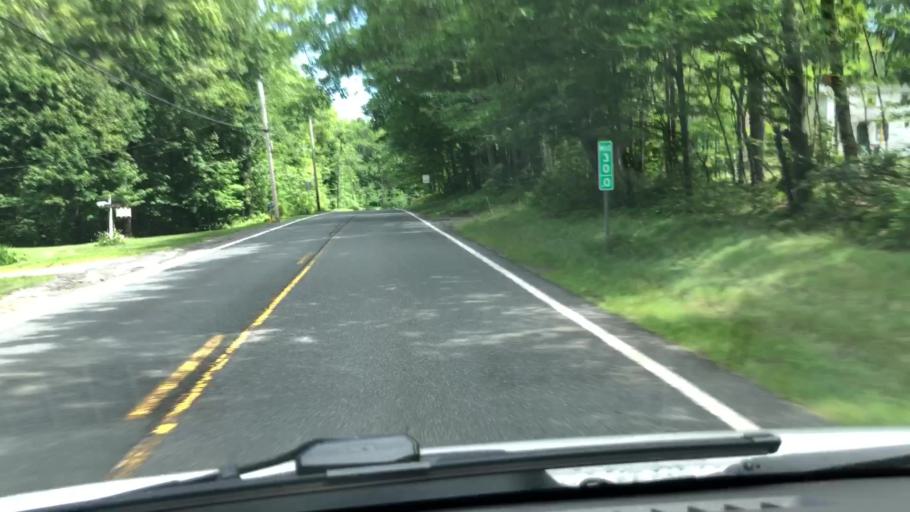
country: US
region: Massachusetts
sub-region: Hampshire County
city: Chesterfield
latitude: 42.4324
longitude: -72.7914
